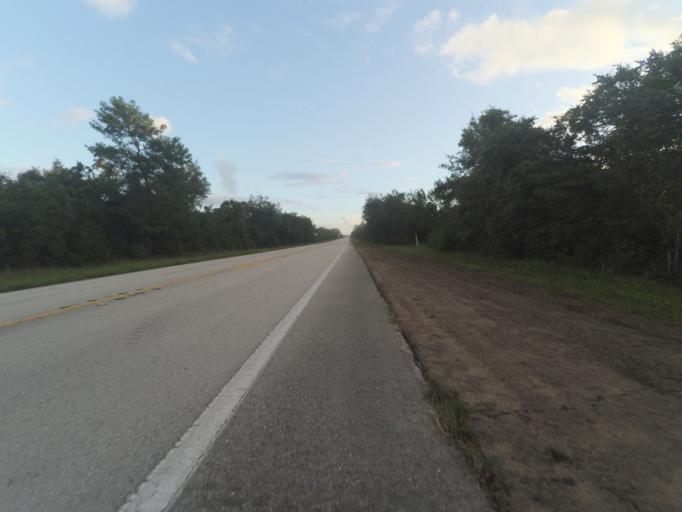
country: US
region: Florida
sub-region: Lake County
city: Astor
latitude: 29.2217
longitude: -81.6460
